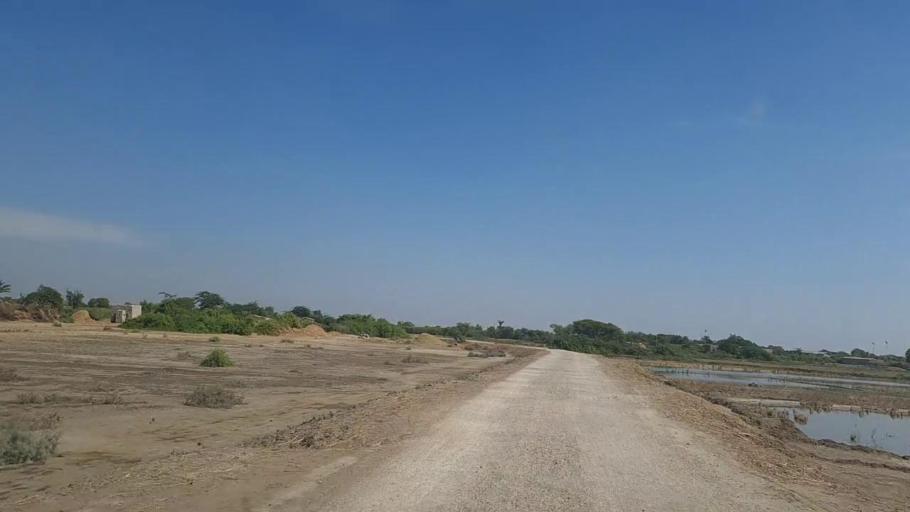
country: PK
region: Sindh
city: Mirpur Batoro
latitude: 24.7475
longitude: 68.2782
